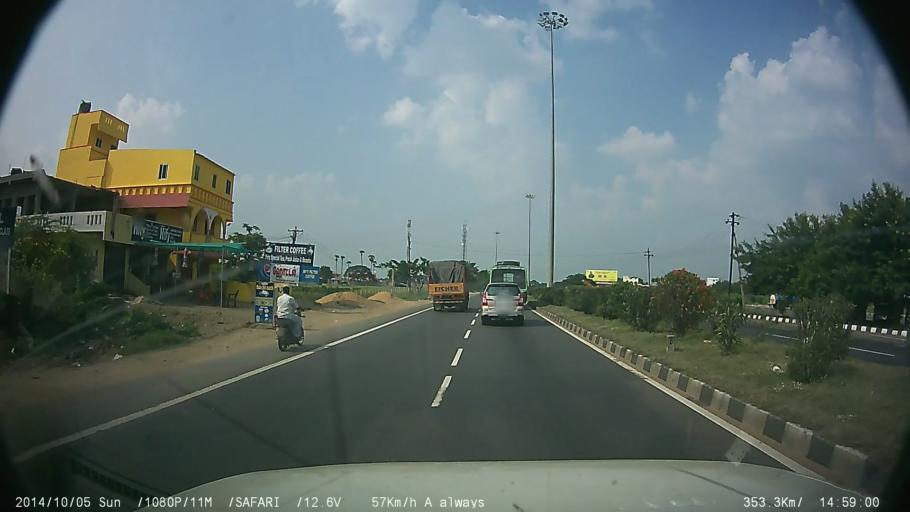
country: IN
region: Tamil Nadu
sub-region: Kancheepuram
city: Madurantakam
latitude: 12.6025
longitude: 79.9201
